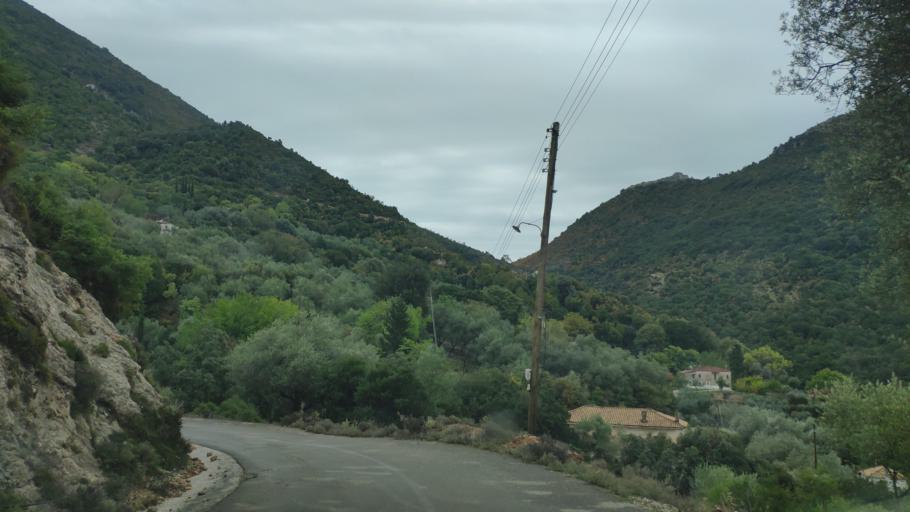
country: GR
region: Epirus
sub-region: Nomos Prevezis
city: Kanalaki
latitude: 39.3467
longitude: 20.6495
